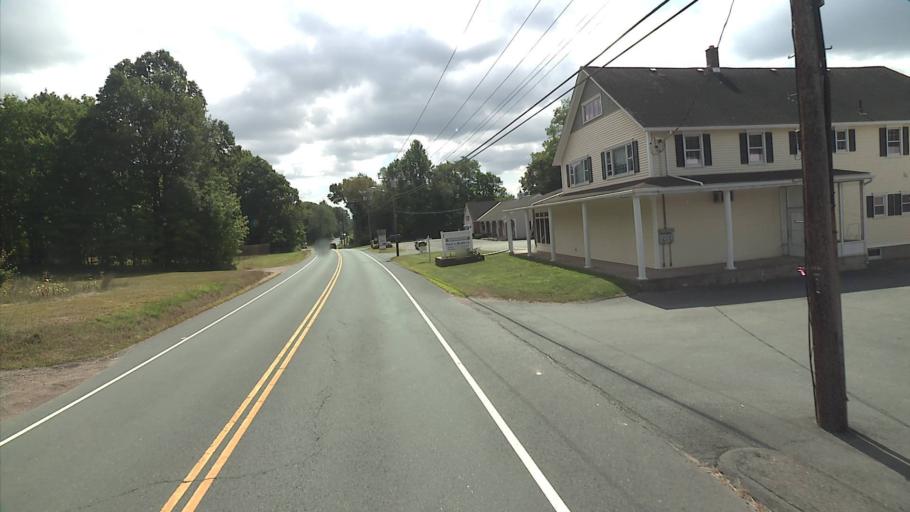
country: US
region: Connecticut
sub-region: Hartford County
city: Salmon Brook
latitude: 41.9391
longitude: -72.7740
